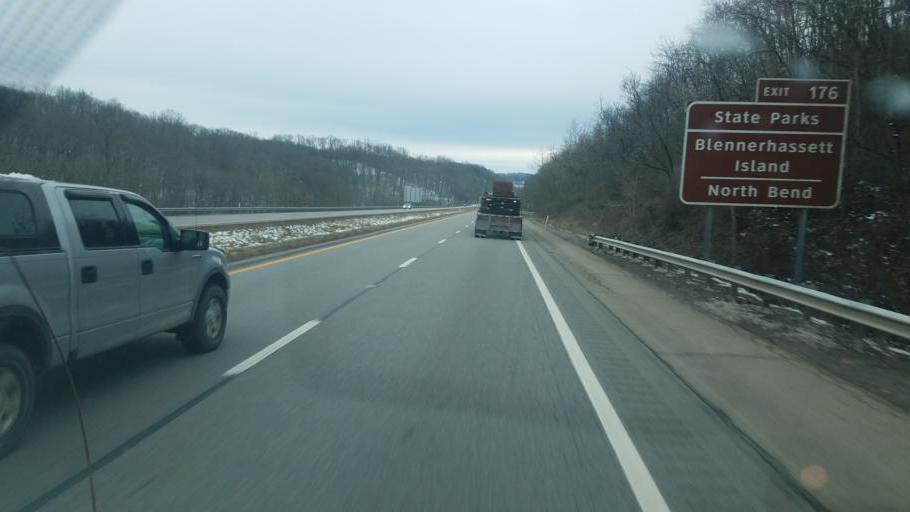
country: US
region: West Virginia
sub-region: Wood County
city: Boaz
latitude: 39.3017
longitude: -81.4901
